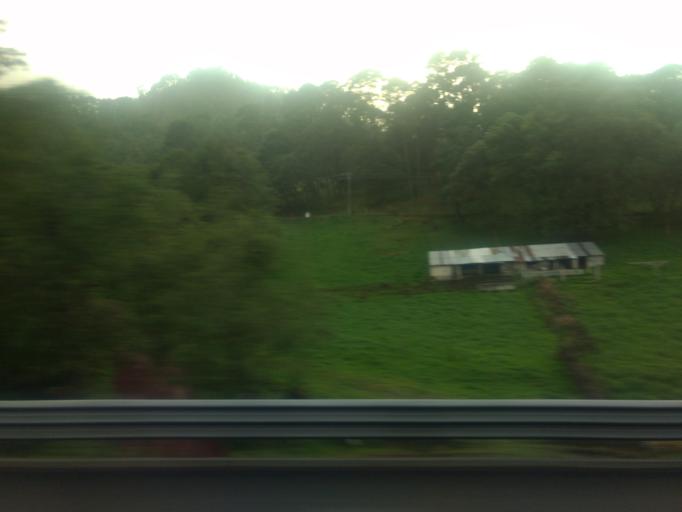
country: MX
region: Veracruz
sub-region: Acajete
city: La Joya
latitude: 19.6291
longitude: -97.0279
